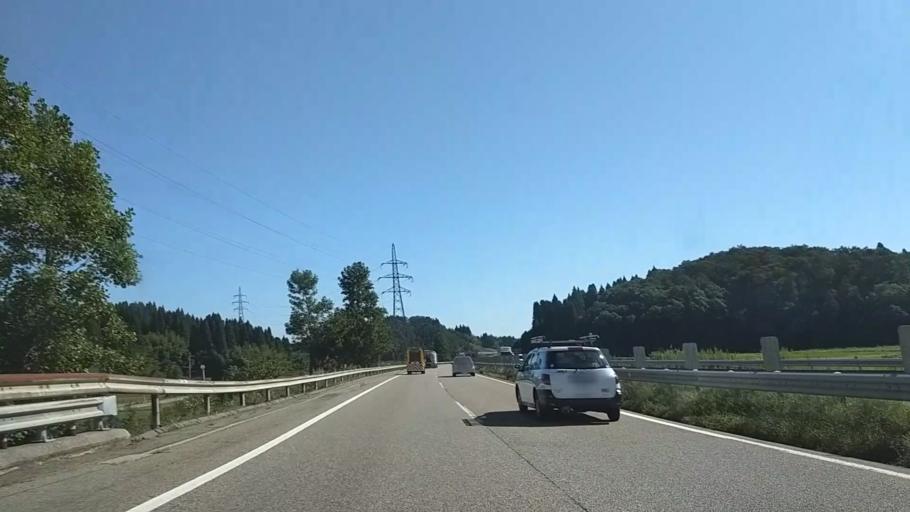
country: JP
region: Toyama
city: Takaoka
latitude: 36.6886
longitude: 137.0594
